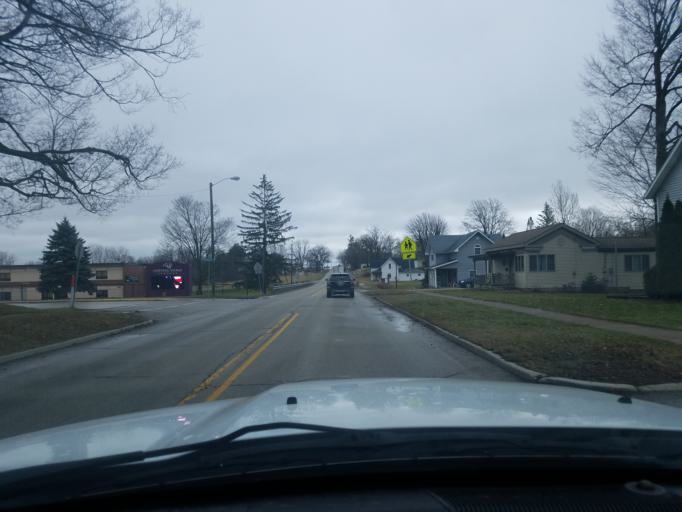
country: US
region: Indiana
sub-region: Noble County
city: Albion
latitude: 41.3957
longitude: -85.4195
